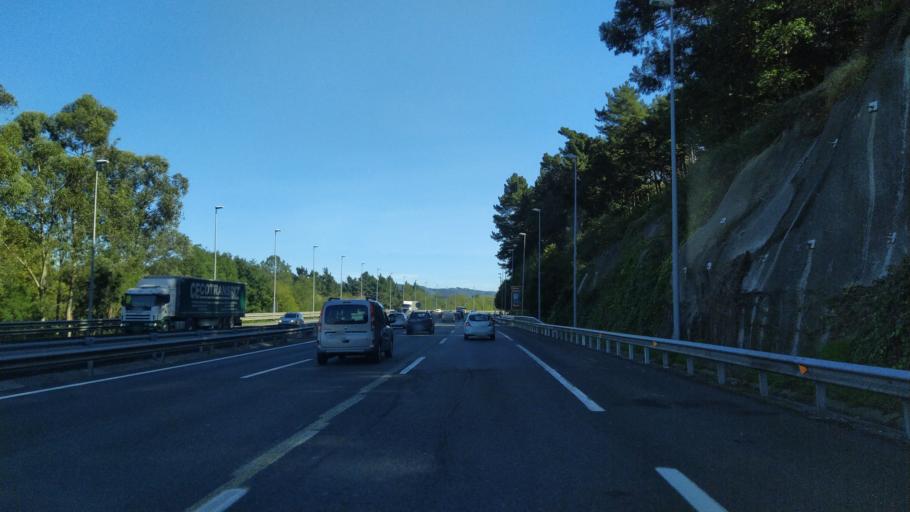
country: ES
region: Basque Country
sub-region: Bizkaia
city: Sondika
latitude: 43.2891
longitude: -2.9109
